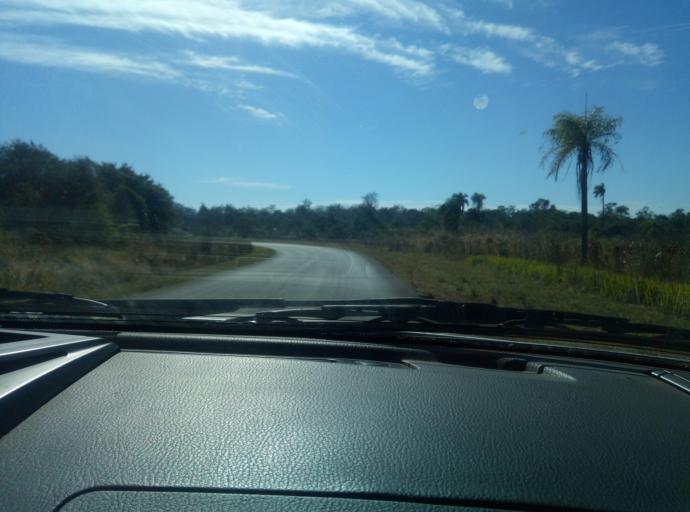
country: PY
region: Caaguazu
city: Carayao
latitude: -25.1807
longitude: -56.3123
